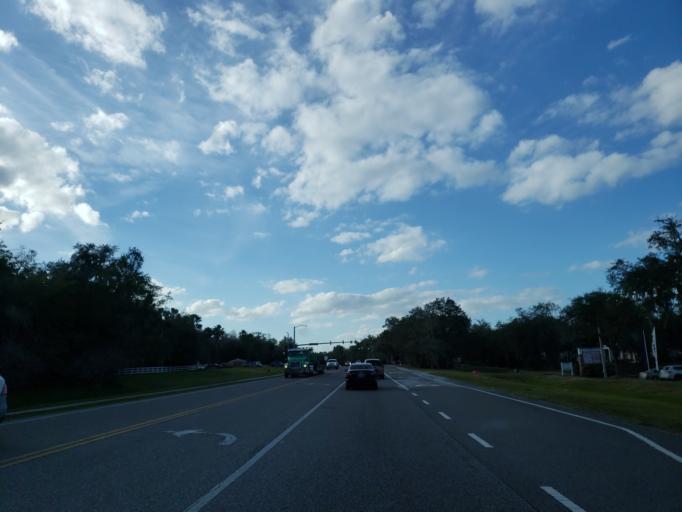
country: US
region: Florida
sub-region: Hillsborough County
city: Fish Hawk
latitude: 27.8524
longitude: -82.2296
